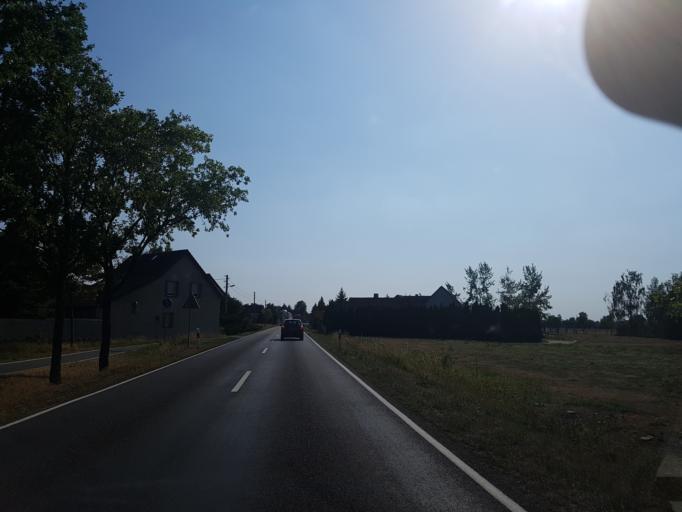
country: DE
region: Saxony-Anhalt
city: Annaburg
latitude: 51.7078
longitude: 13.0218
